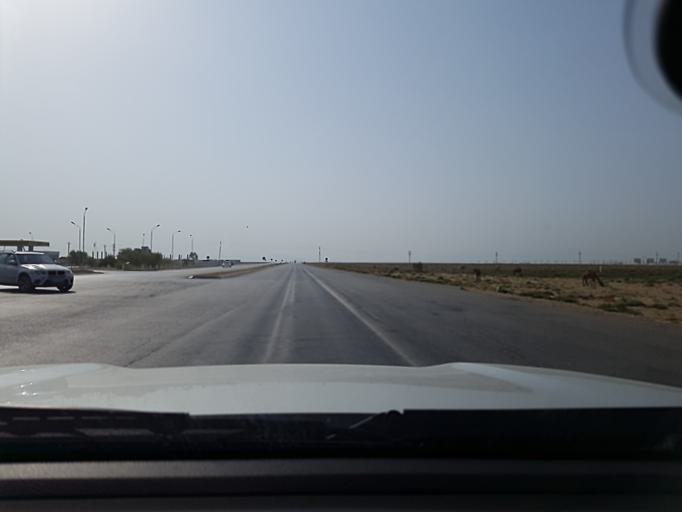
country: TM
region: Balkan
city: Balkanabat
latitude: 39.4901
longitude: 54.3860
